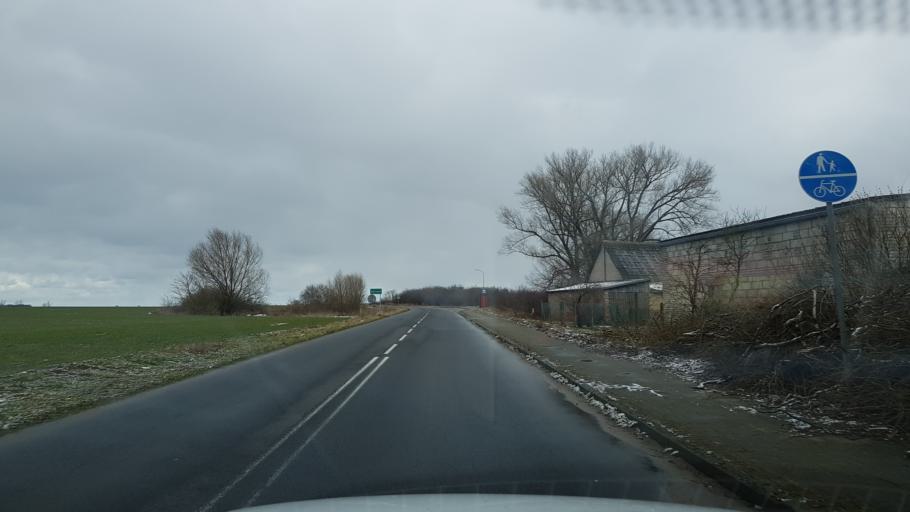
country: PL
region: West Pomeranian Voivodeship
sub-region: Powiat kamienski
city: Kamien Pomorski
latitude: 53.9586
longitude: 14.6854
